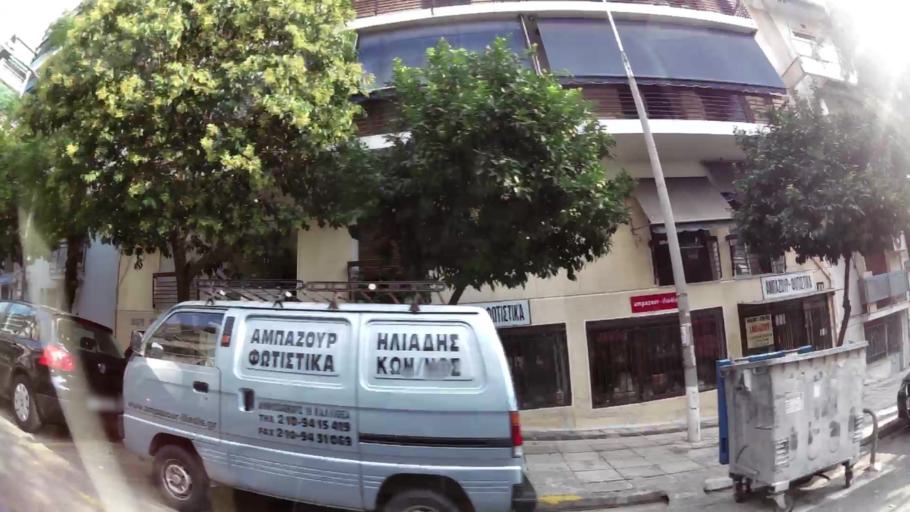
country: GR
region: Attica
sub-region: Nomarchia Athinas
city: Nea Smyrni
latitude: 37.9578
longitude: 23.7126
